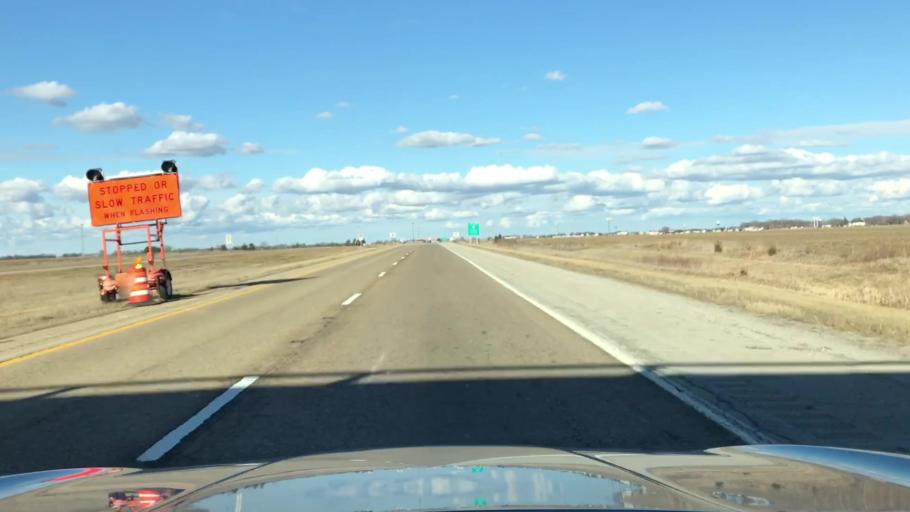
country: US
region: Illinois
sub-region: McLean County
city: Chenoa
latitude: 40.7271
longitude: -88.7370
